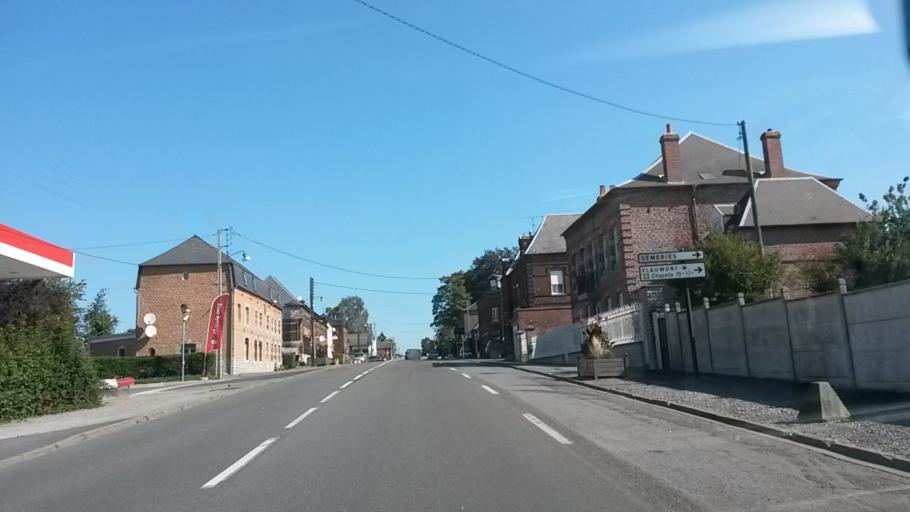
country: FR
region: Nord-Pas-de-Calais
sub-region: Departement du Nord
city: Avesnes-sur-Helpe
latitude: 50.1284
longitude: 3.9368
